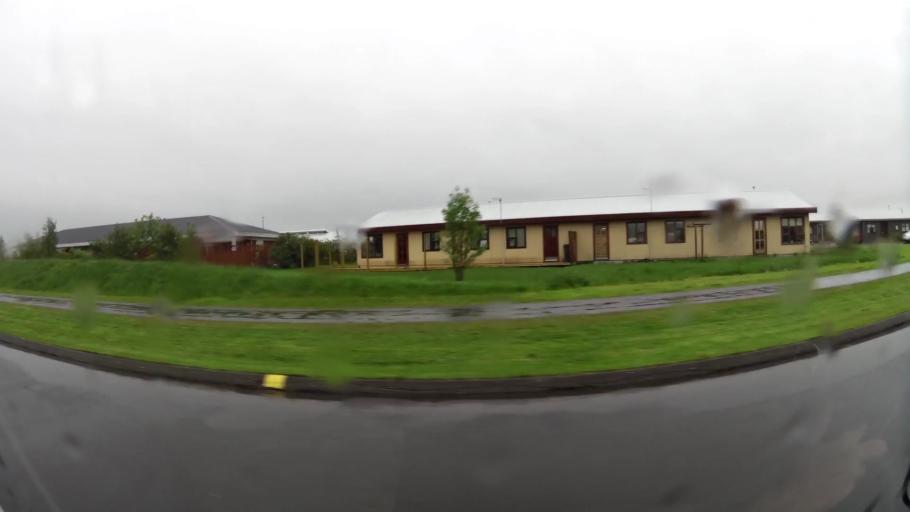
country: IS
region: South
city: Selfoss
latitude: 63.9255
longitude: -20.9929
